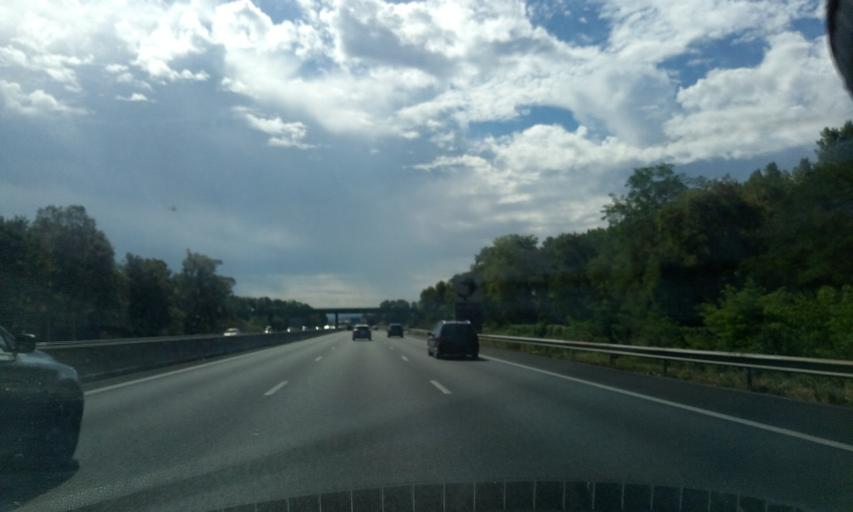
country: FR
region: Rhone-Alpes
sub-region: Departement de l'Isere
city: La Verpilliere
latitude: 45.6363
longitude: 5.1545
